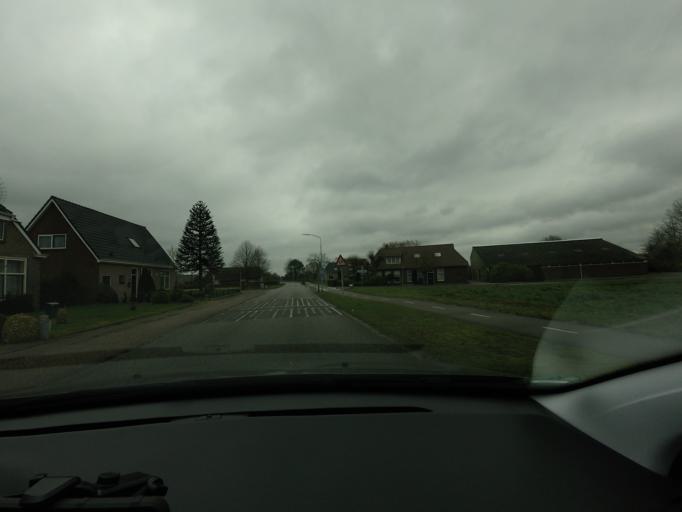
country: NL
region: Drenthe
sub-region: Gemeente Hoogeveen
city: Hoogeveen
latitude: 52.8434
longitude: 6.5344
